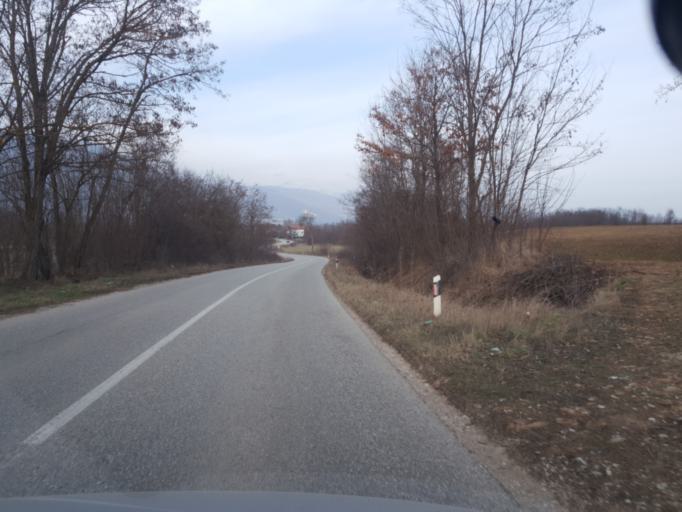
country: XK
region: Pec
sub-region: Komuna e Istogut
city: Istok
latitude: 42.7407
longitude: 20.4833
